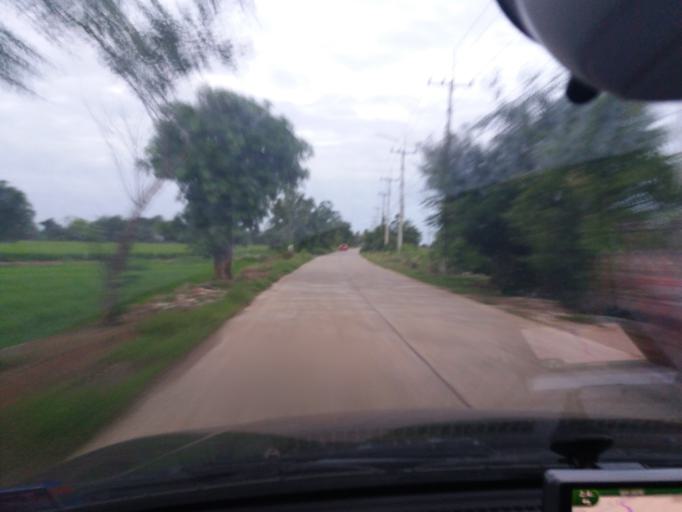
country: TH
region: Suphan Buri
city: Ban Sam Chuk
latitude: 14.7299
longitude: 100.0787
